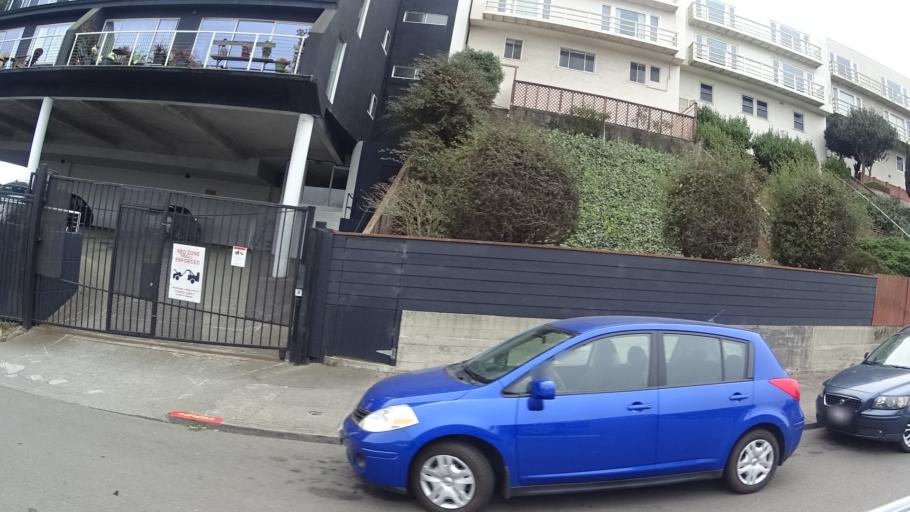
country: US
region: California
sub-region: San Francisco County
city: San Francisco
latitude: 37.7849
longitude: -122.4482
